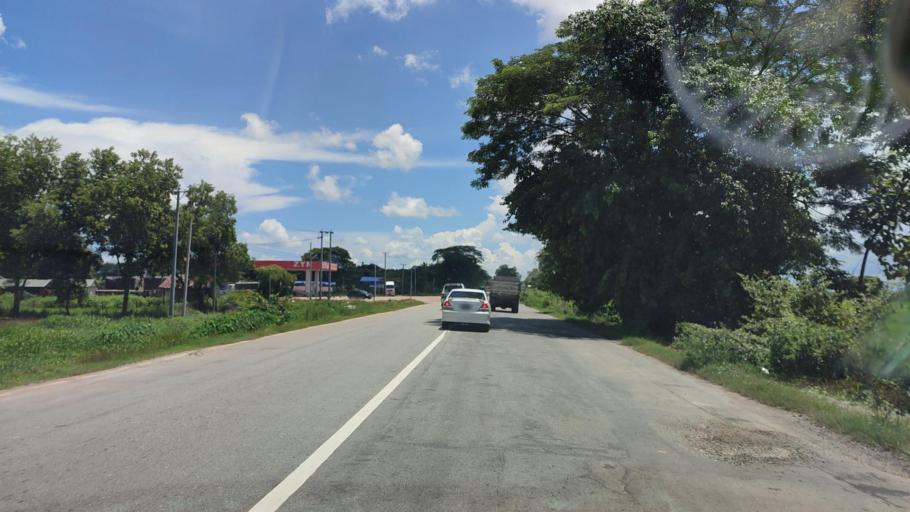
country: MM
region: Bago
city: Nyaunglebin
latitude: 18.2071
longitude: 96.5629
